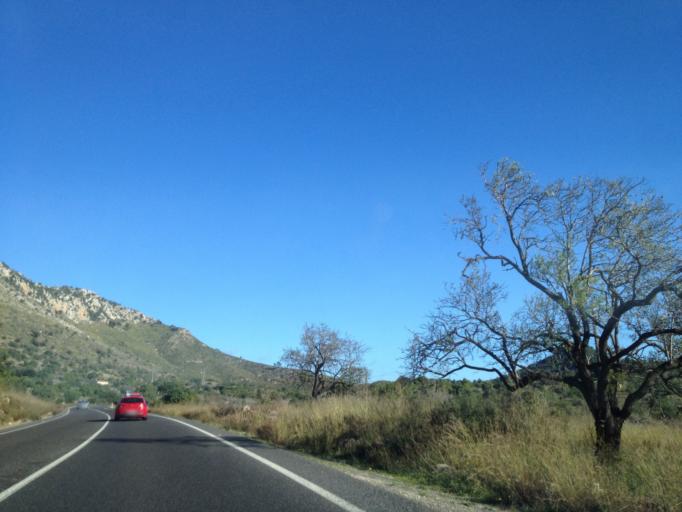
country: ES
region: Balearic Islands
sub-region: Illes Balears
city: Sant Llorenc des Cardassar
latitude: 39.6336
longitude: 3.3016
